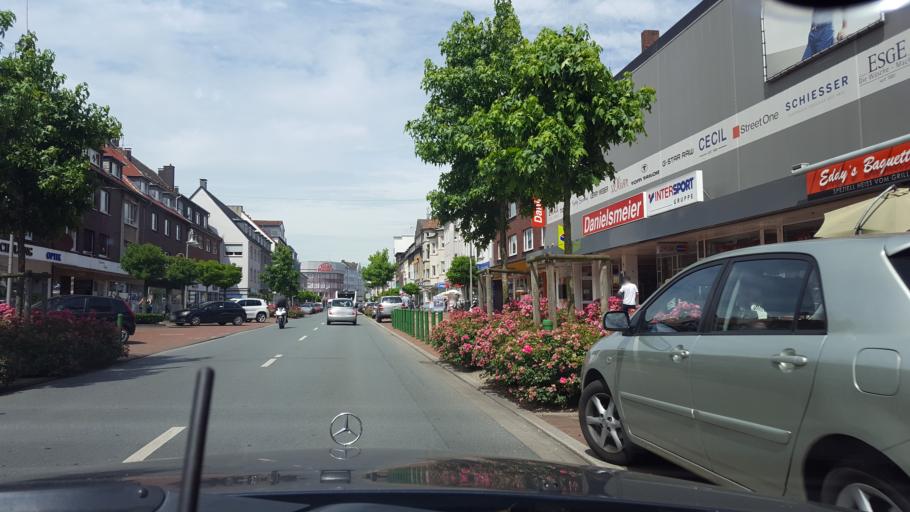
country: DE
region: North Rhine-Westphalia
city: Datteln
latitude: 51.6498
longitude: 7.3388
